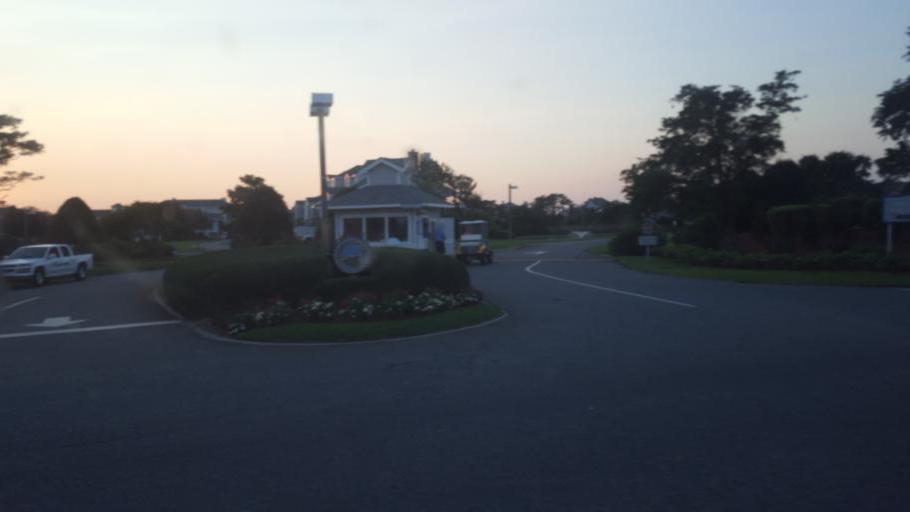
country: US
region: North Carolina
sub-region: Dare County
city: Manteo
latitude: 35.8939
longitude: -75.6448
